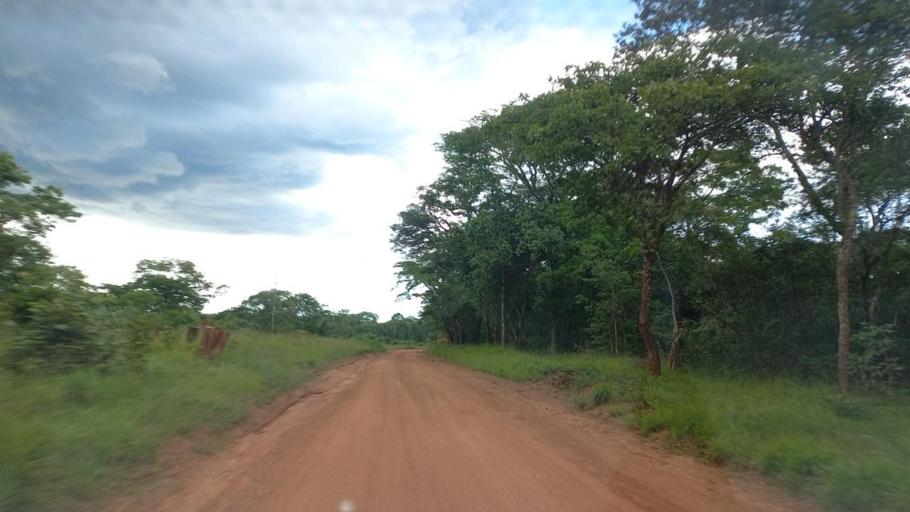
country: ZM
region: North-Western
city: Mwinilunga
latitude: -11.8230
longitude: 24.3665
